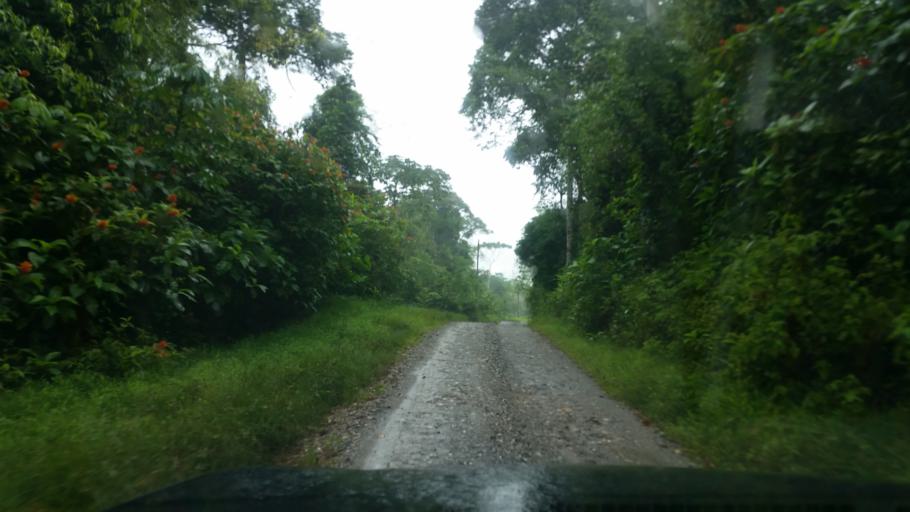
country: NI
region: Atlantico Norte (RAAN)
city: Bonanza
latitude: 14.0756
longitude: -84.6541
